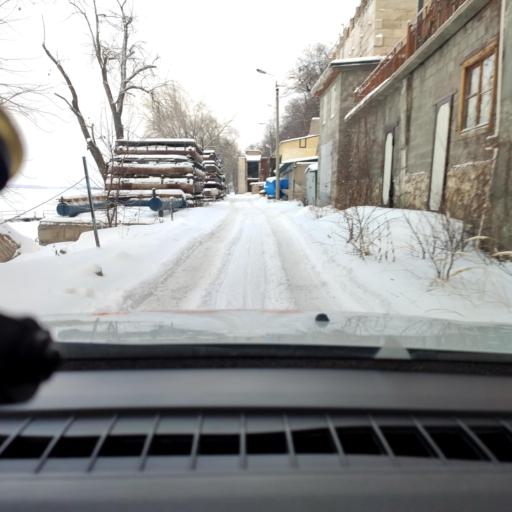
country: RU
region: Samara
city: Samara
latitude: 53.2904
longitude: 50.1920
